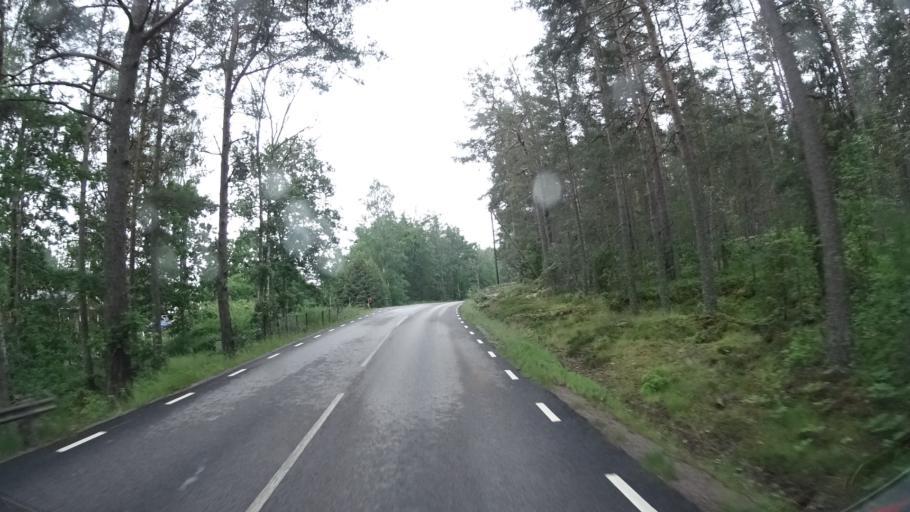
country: SE
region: Kalmar
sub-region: Oskarshamns Kommun
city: Oskarshamn
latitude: 57.3712
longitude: 16.2283
